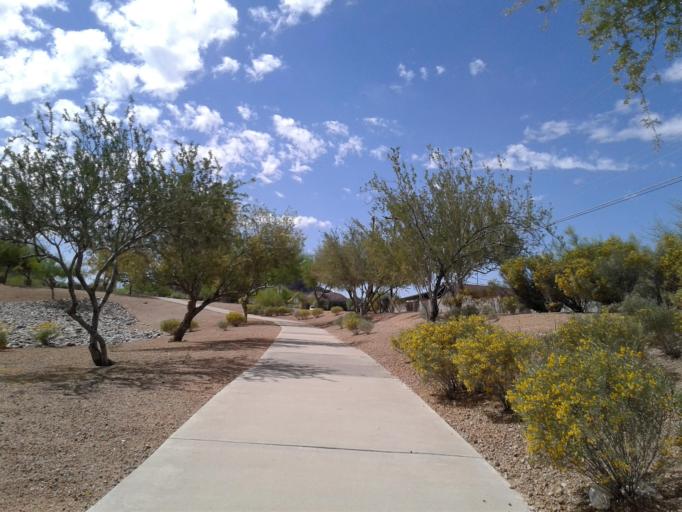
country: US
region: Arizona
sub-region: Maricopa County
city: Tempe Junction
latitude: 33.4683
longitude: -111.9423
